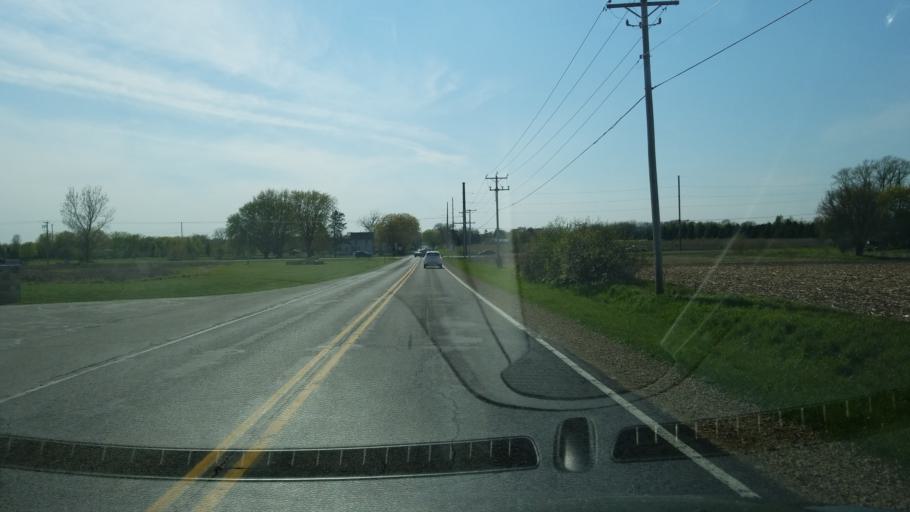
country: US
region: Wisconsin
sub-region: Dane County
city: Fitchburg
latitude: 42.9291
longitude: -89.4359
